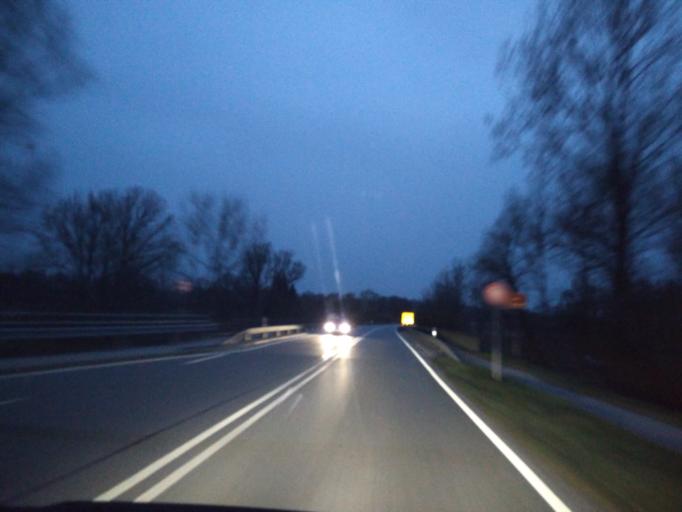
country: DE
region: Bavaria
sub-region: Upper Bavaria
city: Breitbrunn
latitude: 48.0222
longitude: 12.1729
